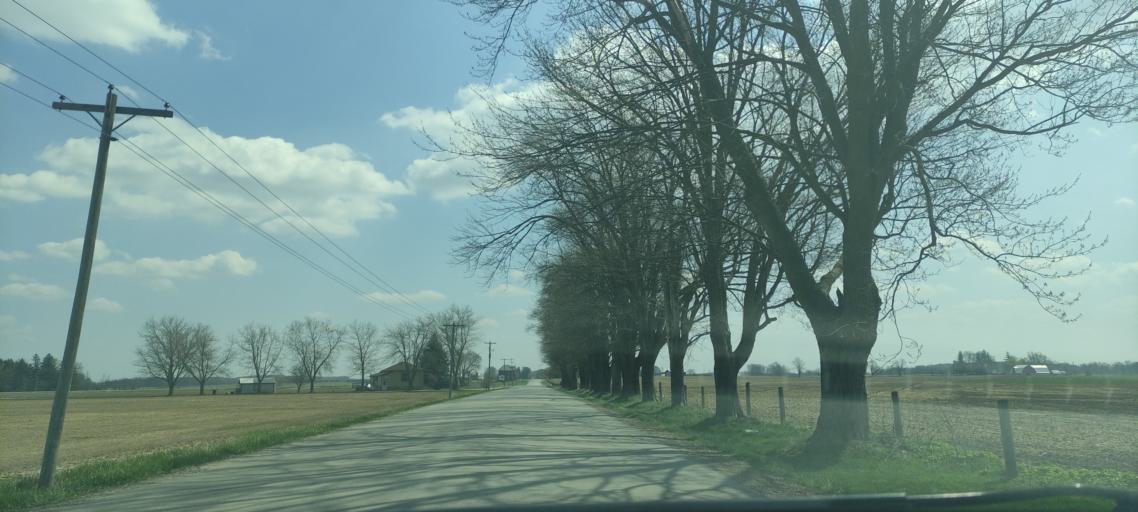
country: CA
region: Ontario
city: Stratford
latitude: 43.3348
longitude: -80.9698
